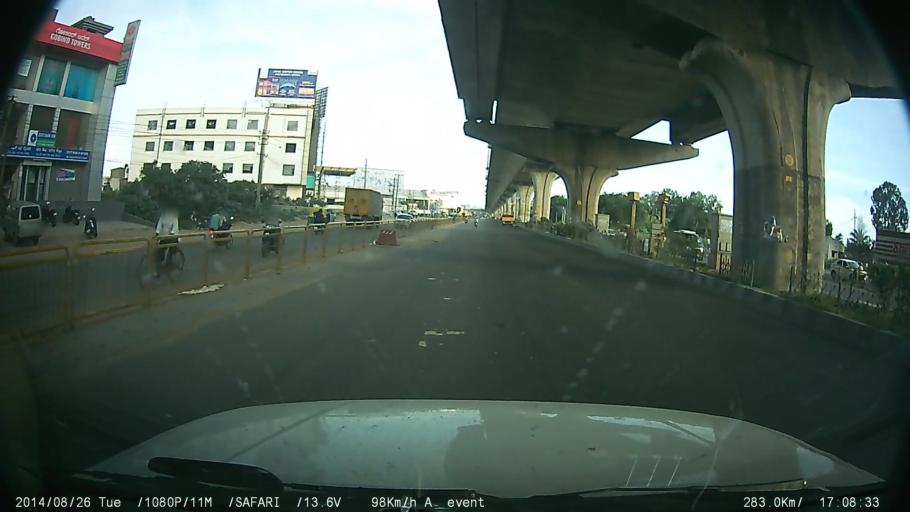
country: IN
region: Karnataka
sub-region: Bangalore Urban
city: Bangalore
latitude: 12.8852
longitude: 77.6426
